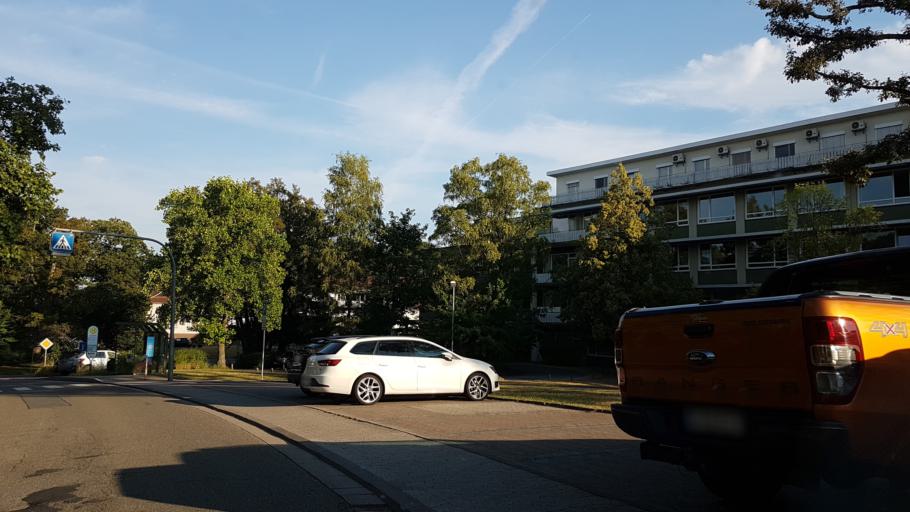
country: DE
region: Saarland
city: Homburg
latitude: 49.3076
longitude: 7.3425
